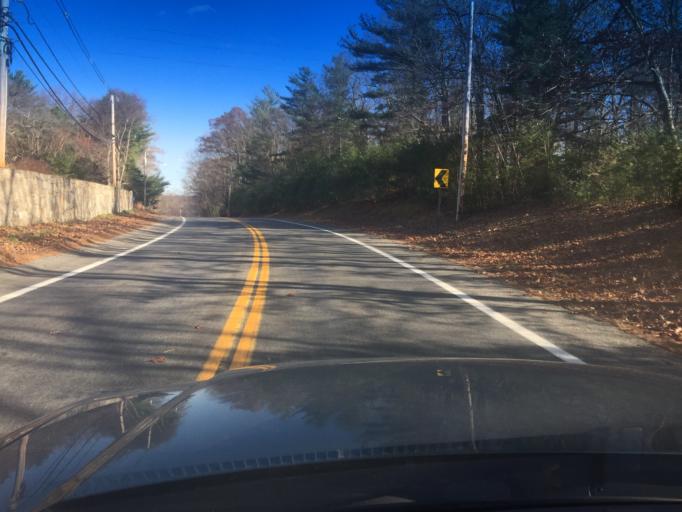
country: US
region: Rhode Island
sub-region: Providence County
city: North Scituate
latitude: 41.8634
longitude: -71.5857
